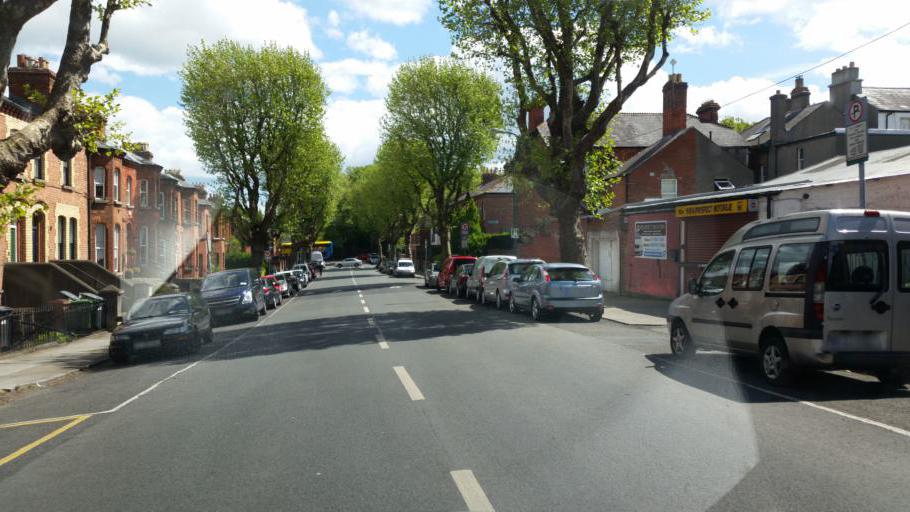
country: IE
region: Leinster
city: Drumcondra
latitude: 53.3673
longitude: -6.2579
